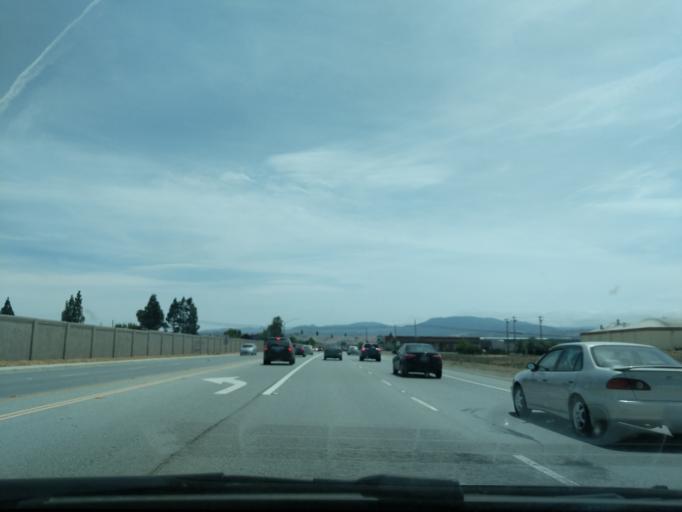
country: US
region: California
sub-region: San Benito County
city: Hollister
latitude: 36.8495
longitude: -121.3904
